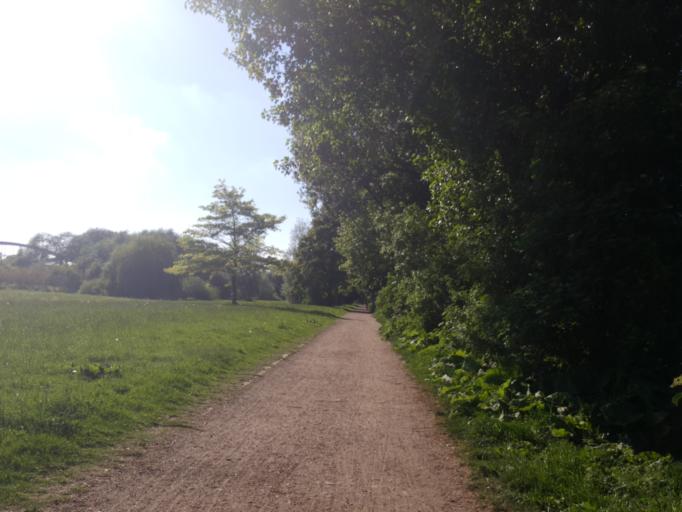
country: DE
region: Hamburg
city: Rothenburgsort
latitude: 53.5310
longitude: 10.0354
